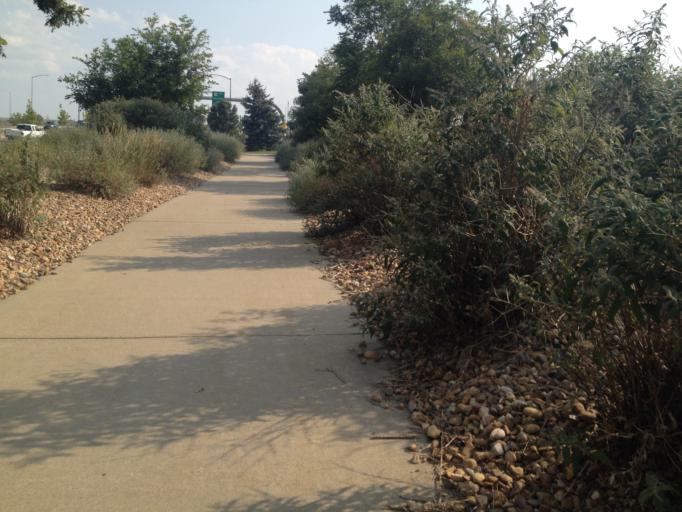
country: US
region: Colorado
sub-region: Boulder County
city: Superior
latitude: 39.9607
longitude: -105.1656
